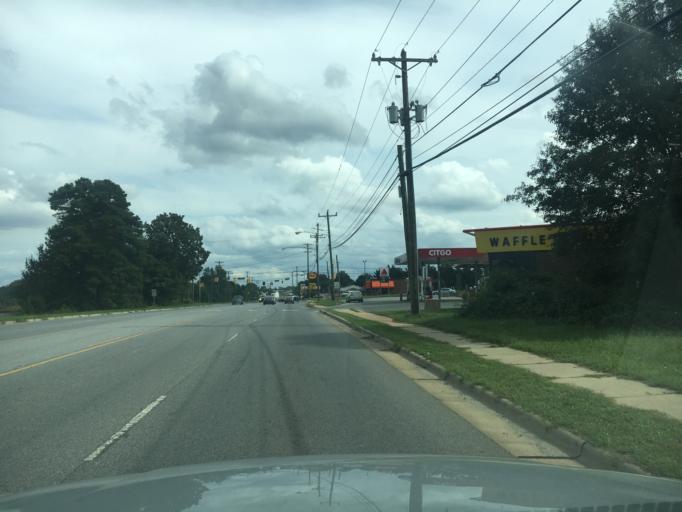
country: US
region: North Carolina
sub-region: Gaston County
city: Bessemer City
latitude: 35.2796
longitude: -81.2350
